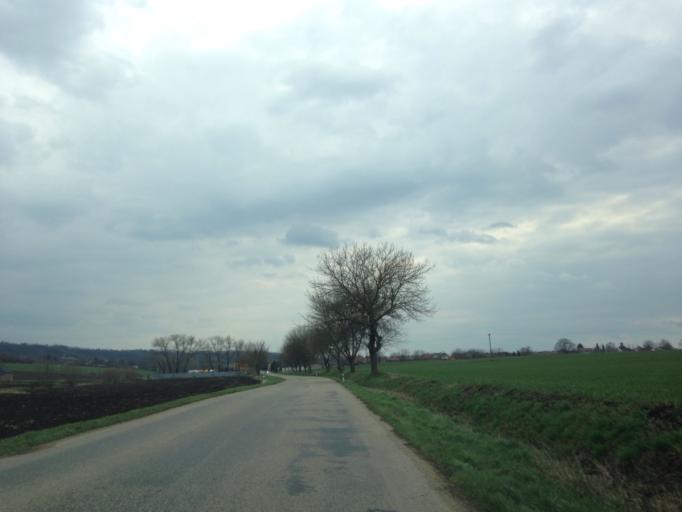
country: SK
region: Nitriansky
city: Svodin
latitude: 47.9692
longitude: 18.4084
